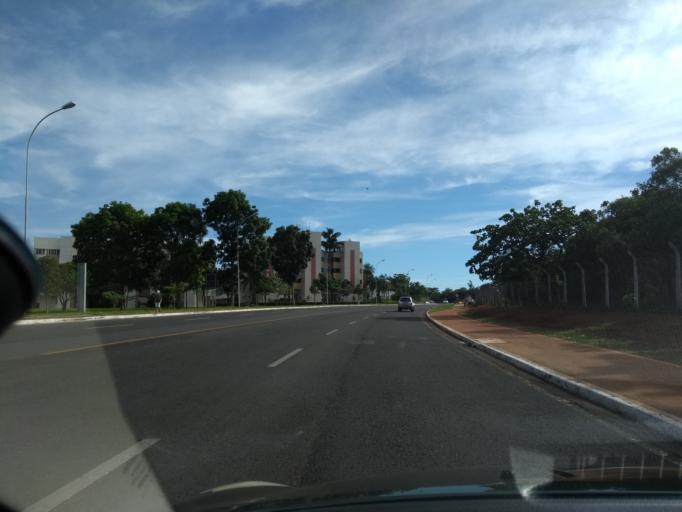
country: BR
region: Federal District
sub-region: Brasilia
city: Brasilia
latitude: -15.7868
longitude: -47.9280
